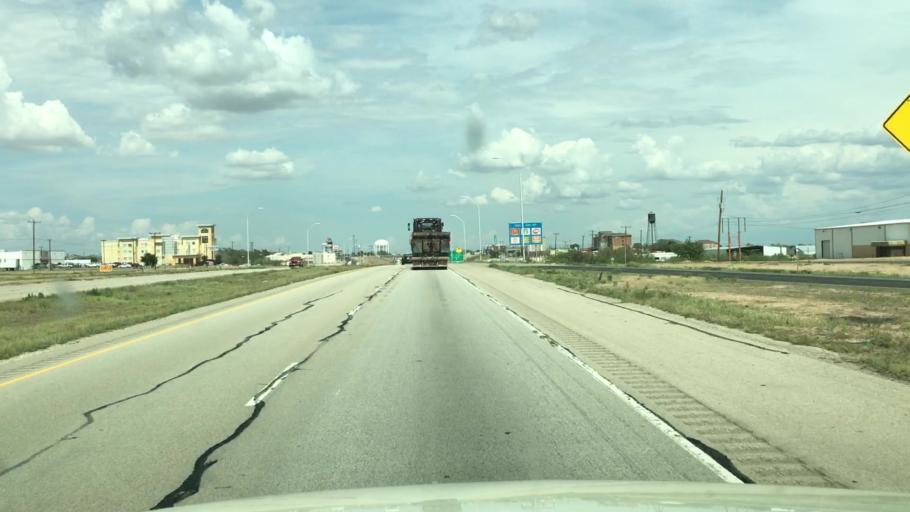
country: US
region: Texas
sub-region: Howard County
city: Big Spring
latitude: 32.2612
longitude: -101.5008
